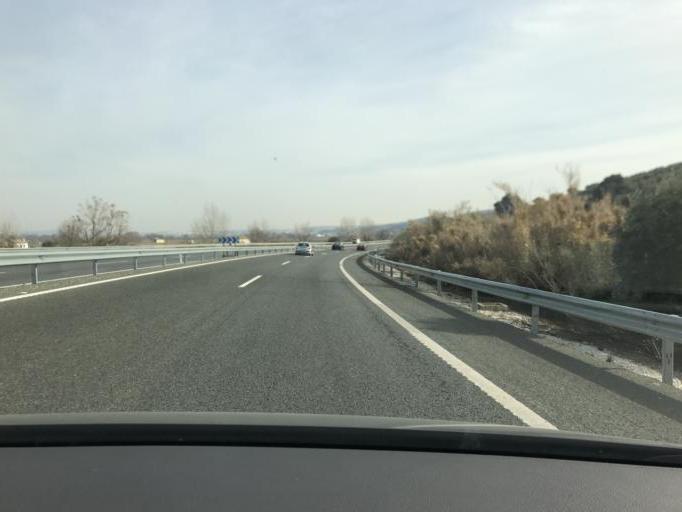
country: ES
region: Andalusia
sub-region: Provincia de Granada
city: Salar
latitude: 37.1810
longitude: -4.0769
